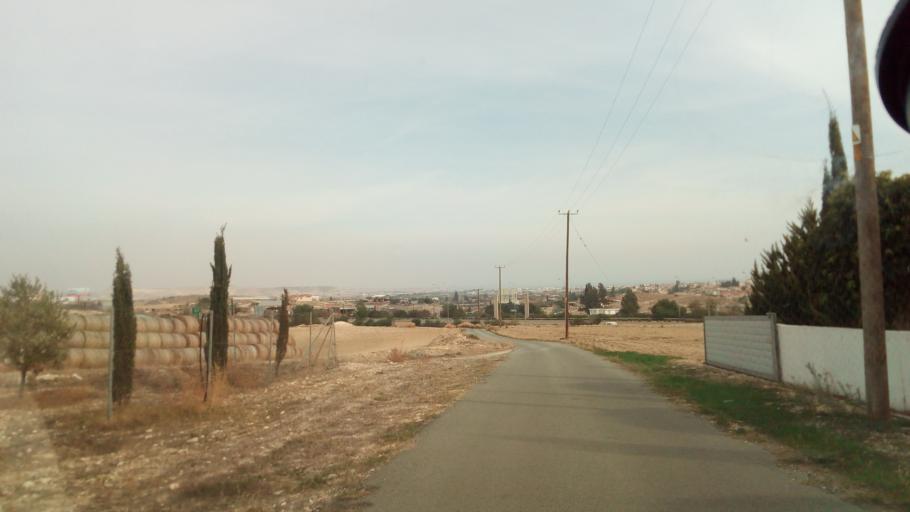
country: CY
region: Larnaka
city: Aradippou
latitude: 34.9557
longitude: 33.5751
